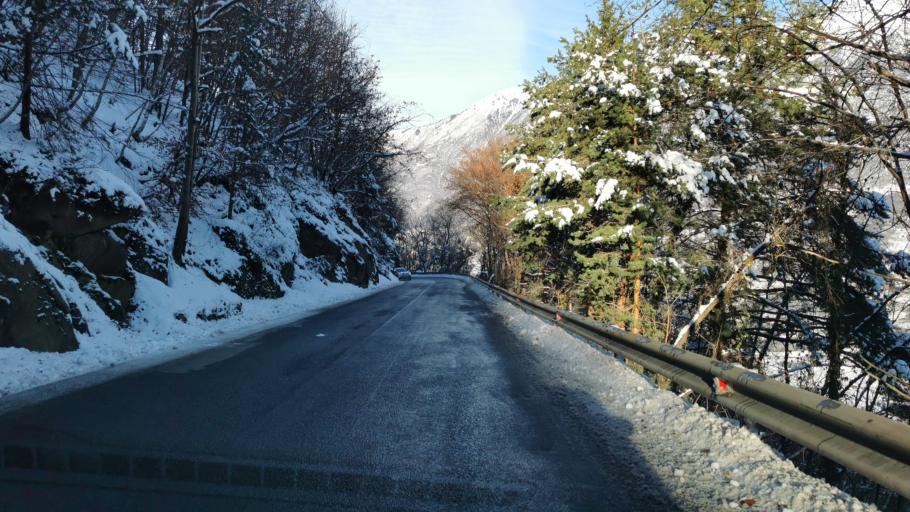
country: IT
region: Lombardy
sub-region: Provincia di Sondrio
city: Cosio Valtellino
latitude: 46.1224
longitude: 9.5592
